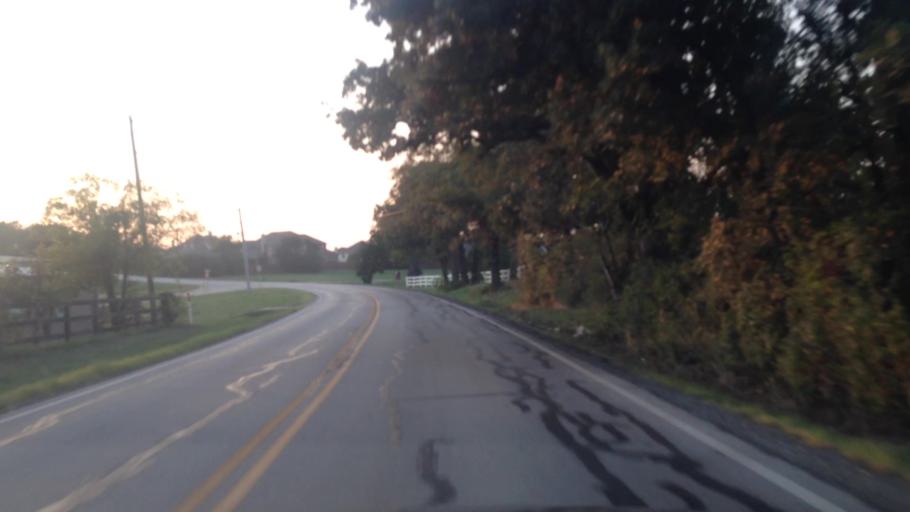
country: US
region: Texas
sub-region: Tarrant County
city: Kennedale
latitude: 32.6368
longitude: -97.2050
